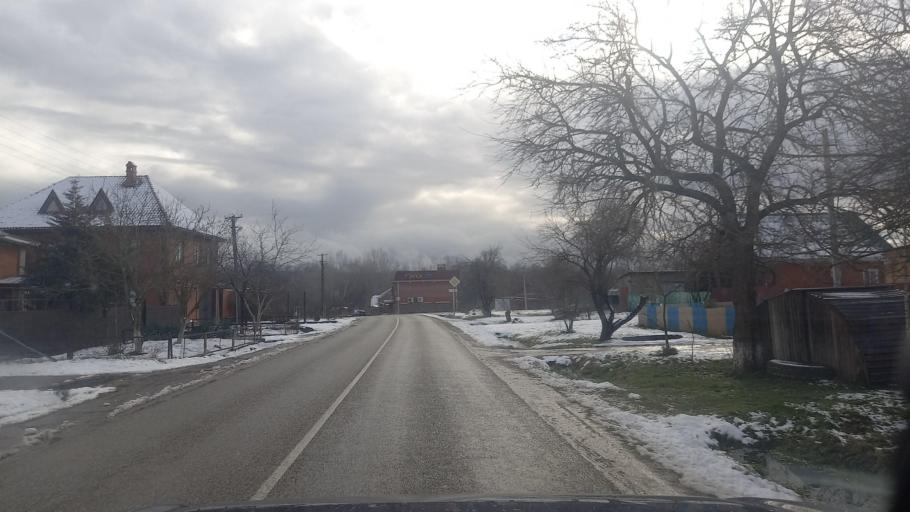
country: RU
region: Krasnodarskiy
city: Smolenskaya
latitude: 44.7743
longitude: 38.8459
